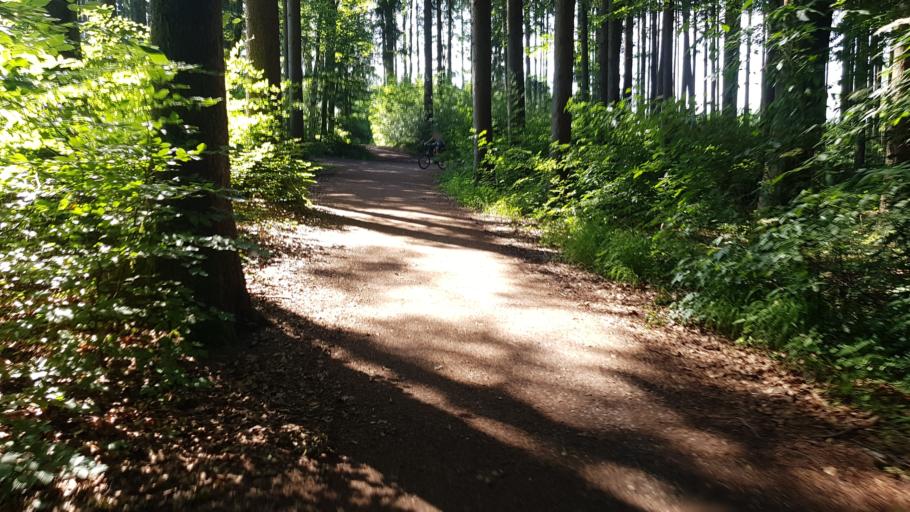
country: DE
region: Bavaria
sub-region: Upper Bavaria
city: Starnberg
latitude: 48.0181
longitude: 11.3725
